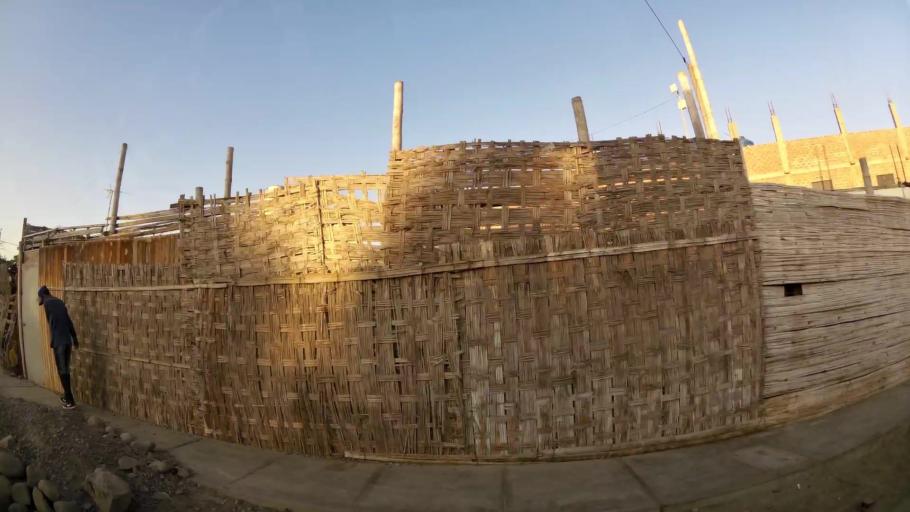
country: PE
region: Ica
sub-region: Provincia de Pisco
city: Villa Tupac Amaru
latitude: -13.7034
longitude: -76.1540
